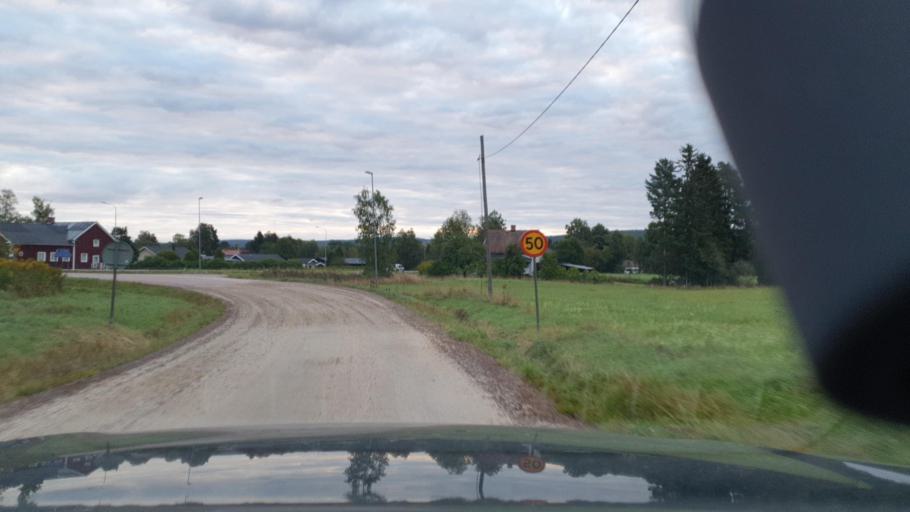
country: SE
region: Vaermland
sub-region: Munkfors Kommun
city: Munkfors
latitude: 59.8310
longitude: 13.5136
